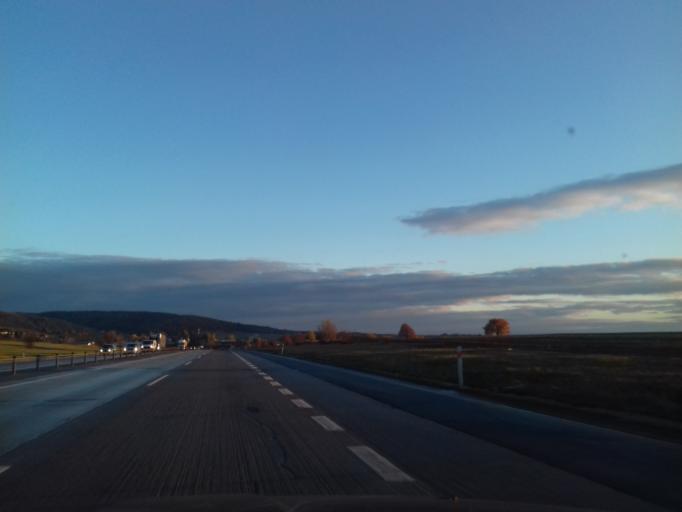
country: CZ
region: South Moravian
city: Pustimer
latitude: 49.3088
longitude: 17.0318
